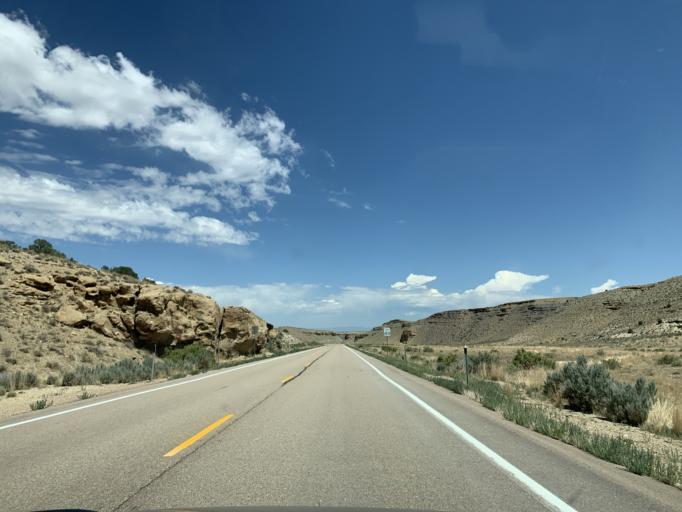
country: US
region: Utah
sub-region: Duchesne County
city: Duchesne
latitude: 39.9999
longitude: -110.1536
